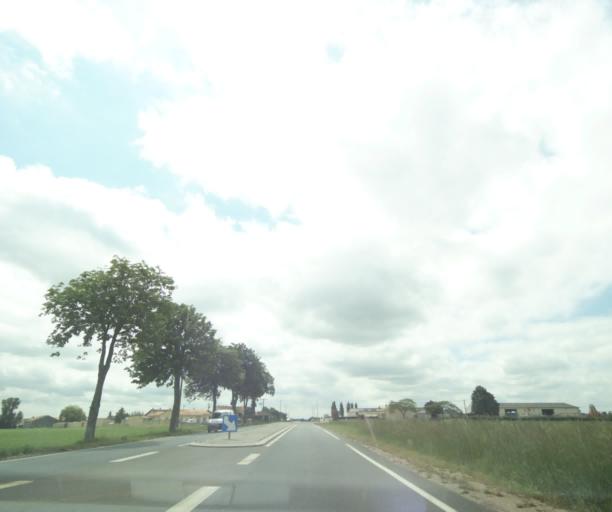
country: FR
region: Poitou-Charentes
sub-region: Departement des Deux-Sevres
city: Saint-Jean-de-Thouars
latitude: 46.9263
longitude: -0.1985
